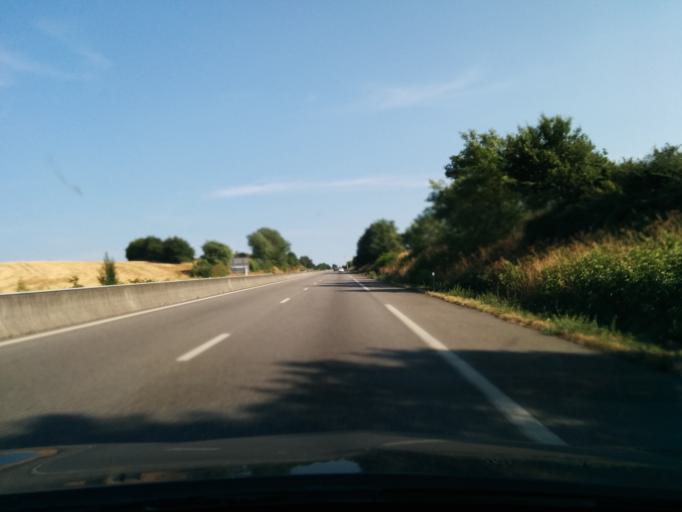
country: FR
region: Limousin
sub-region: Departement de la Haute-Vienne
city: Pierre-Buffiere
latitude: 45.7200
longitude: 1.3515
